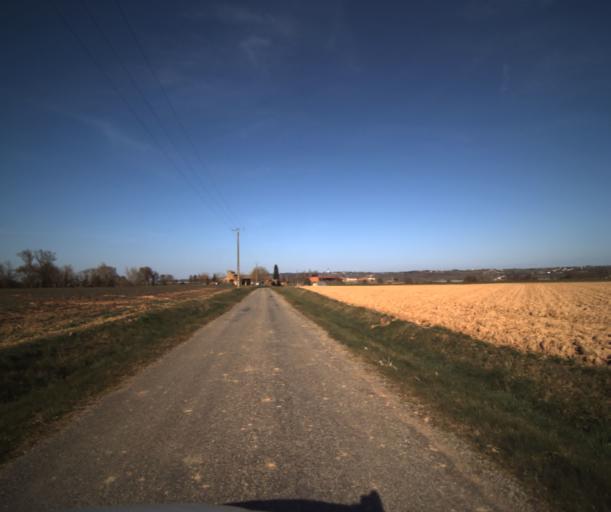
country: FR
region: Midi-Pyrenees
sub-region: Departement du Tarn-et-Garonne
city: Corbarieu
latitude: 43.9339
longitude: 1.3373
